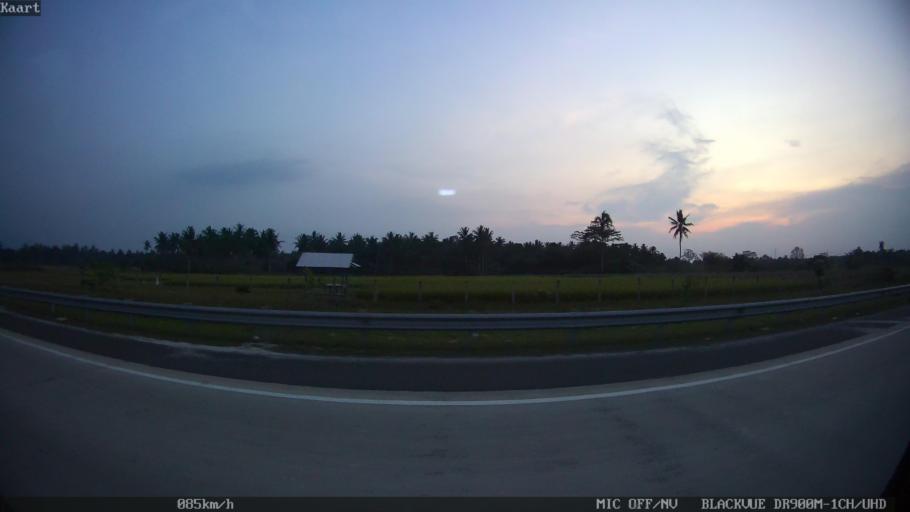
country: ID
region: Lampung
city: Sidorejo
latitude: -5.6449
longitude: 105.5766
